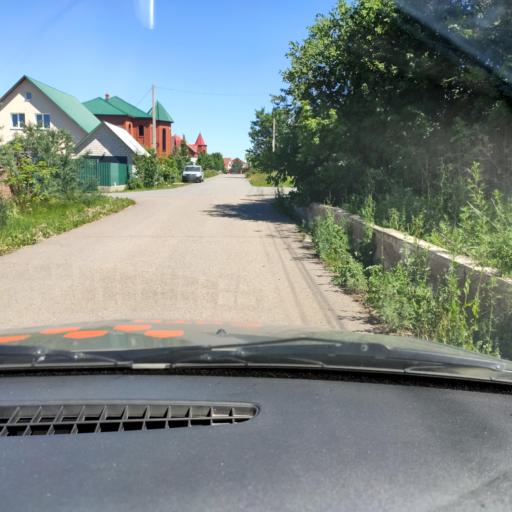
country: RU
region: Bashkortostan
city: Ufa
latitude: 54.6014
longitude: 55.9440
